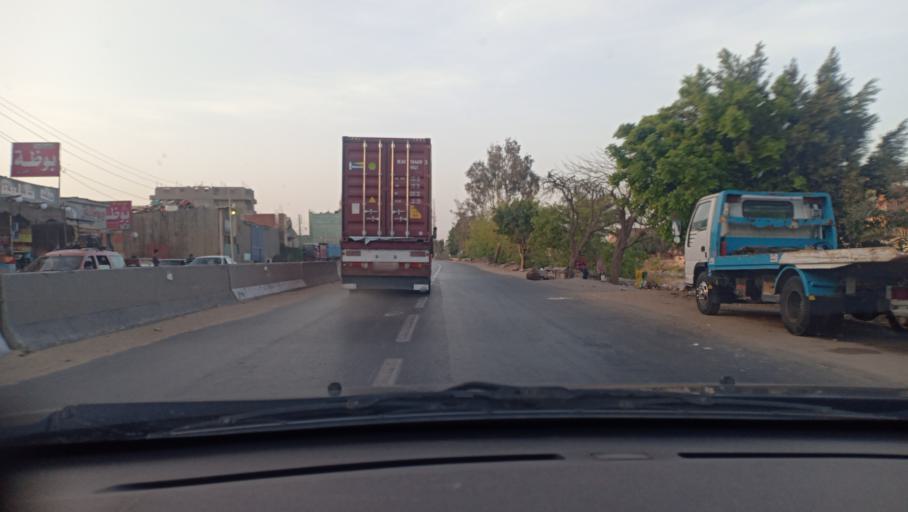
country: EG
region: Muhafazat al Gharbiyah
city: Zifta
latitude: 30.6413
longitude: 31.2816
